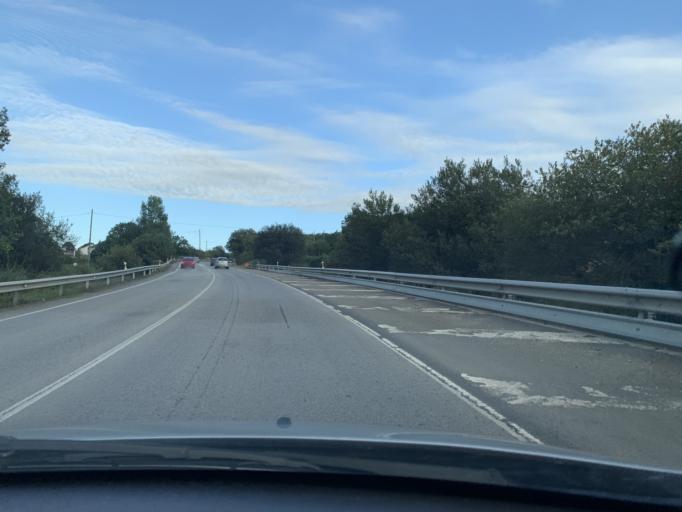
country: ES
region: Galicia
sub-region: Provincia de Lugo
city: Foz
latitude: 43.5553
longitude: -7.2692
